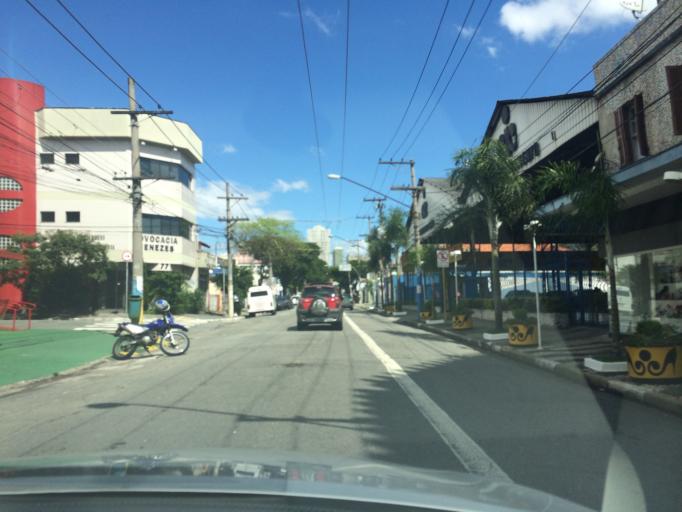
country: BR
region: Sao Paulo
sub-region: Guarulhos
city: Guarulhos
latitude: -23.5325
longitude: -46.5609
